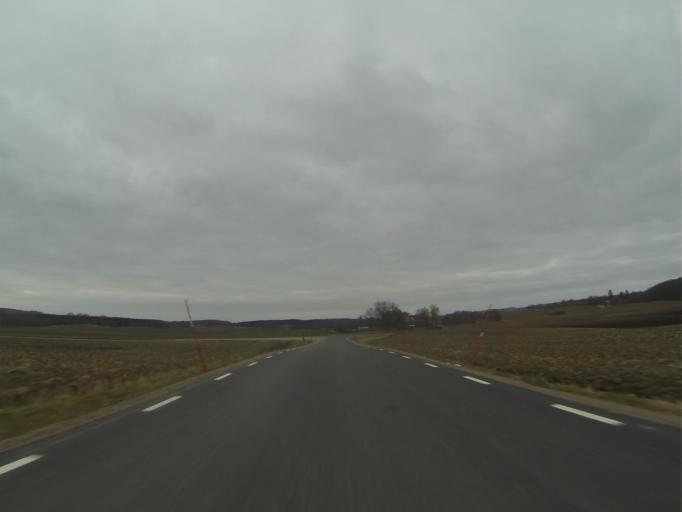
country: SE
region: Skane
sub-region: Skurups Kommun
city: Skurup
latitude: 55.5359
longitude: 13.4426
